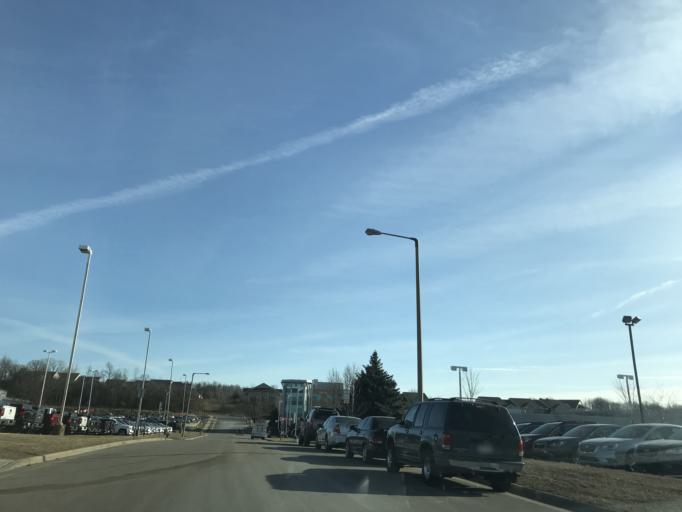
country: US
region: Wisconsin
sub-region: Dane County
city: Sun Prairie
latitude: 43.1416
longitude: -89.2886
